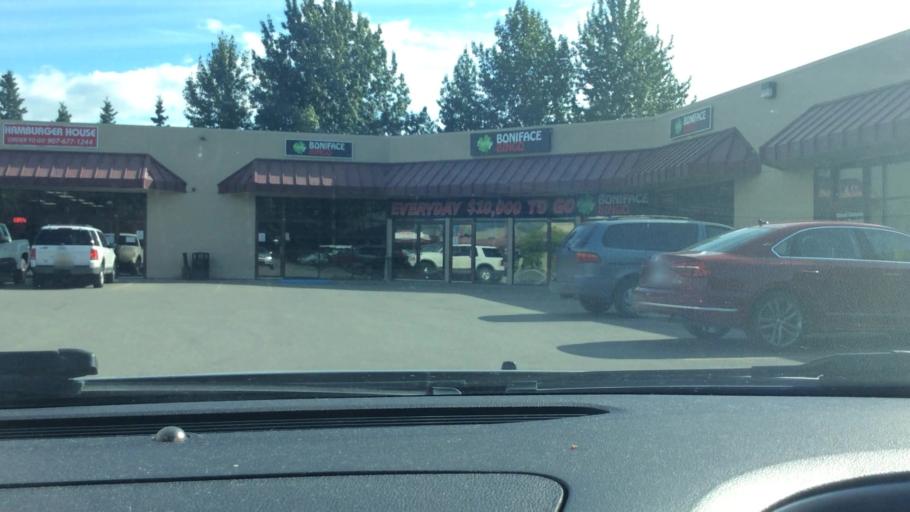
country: US
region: Alaska
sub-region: Anchorage Municipality
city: Anchorage
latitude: 61.2213
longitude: -149.7806
